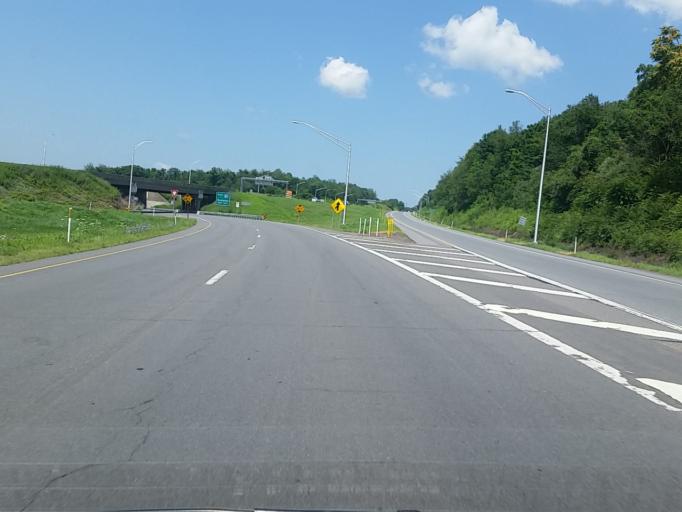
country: US
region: Pennsylvania
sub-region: Columbia County
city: Mifflinville
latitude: 41.0352
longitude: -76.3361
